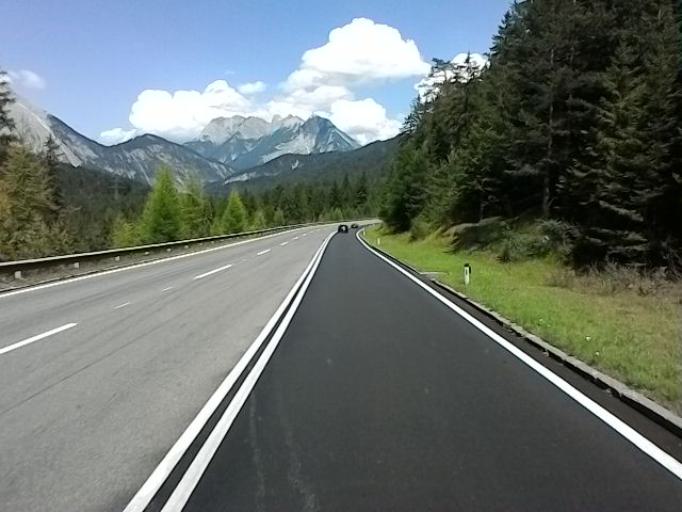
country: AT
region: Tyrol
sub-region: Politischer Bezirk Innsbruck Land
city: Seefeld in Tirol
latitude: 47.3490
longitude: 11.2141
